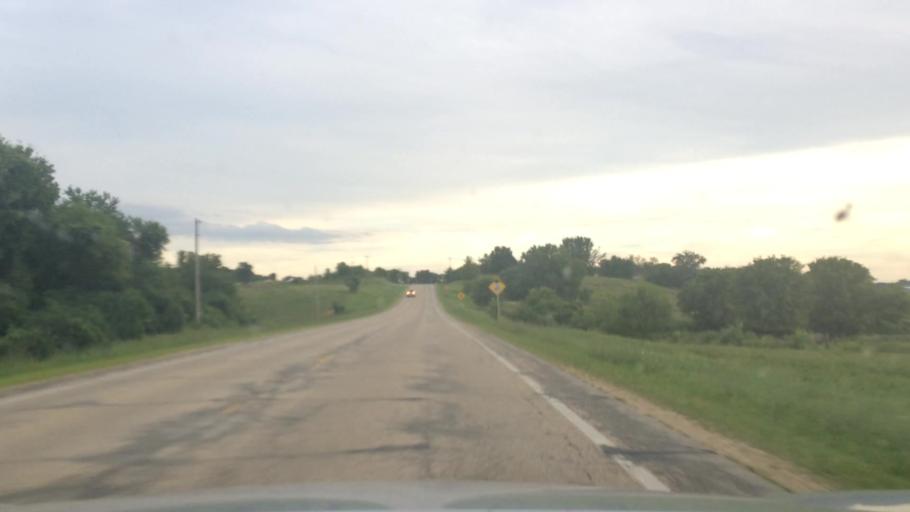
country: US
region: Wisconsin
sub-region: Dane County
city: Waunakee
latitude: 43.2055
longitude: -89.5496
